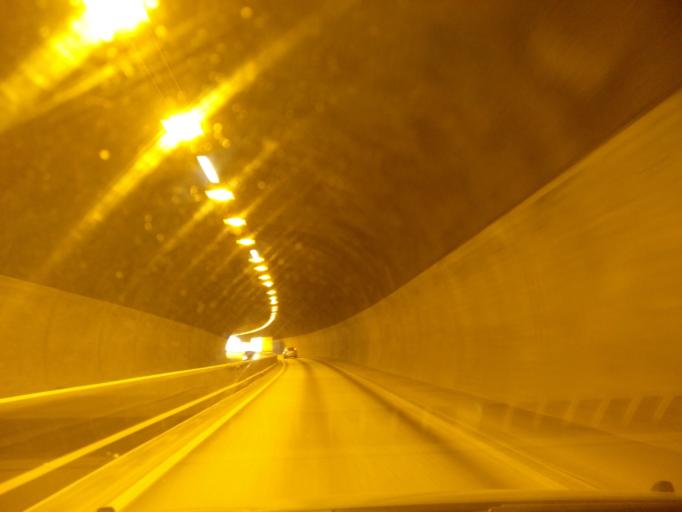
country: NO
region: Rogaland
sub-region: Tysvaer
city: Aksdal
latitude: 59.5072
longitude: 5.6156
